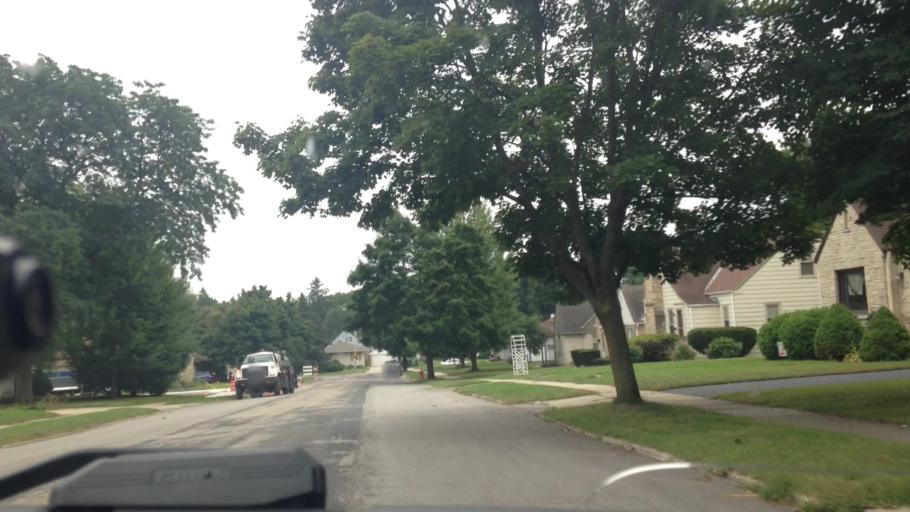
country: US
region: Wisconsin
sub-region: Waukesha County
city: Menomonee Falls
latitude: 43.1767
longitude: -88.1211
